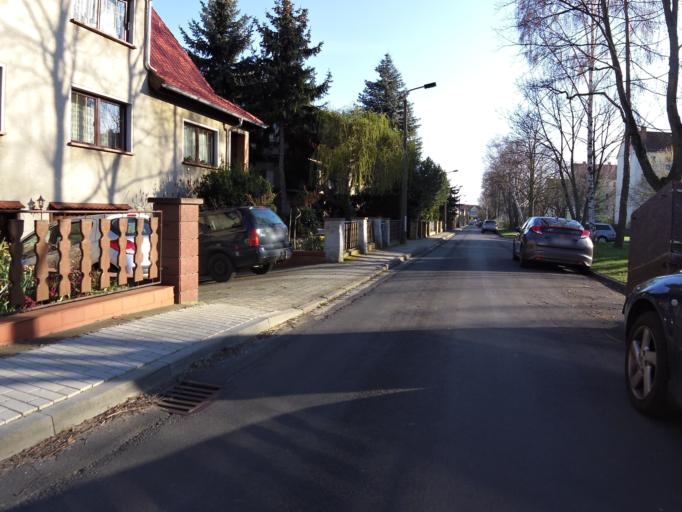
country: DE
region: Saxony
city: Markkleeberg
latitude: 51.2987
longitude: 12.3224
